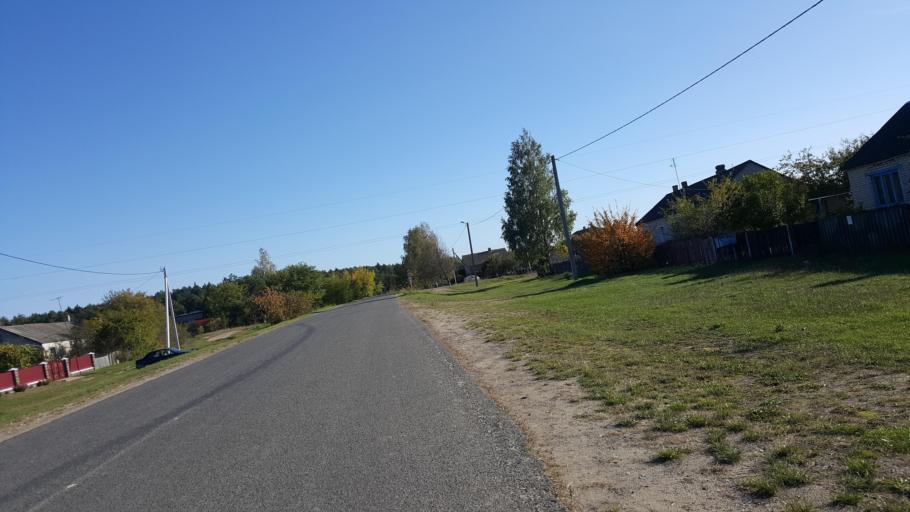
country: BY
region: Brest
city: Kamyanyets
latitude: 52.4141
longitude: 23.8889
